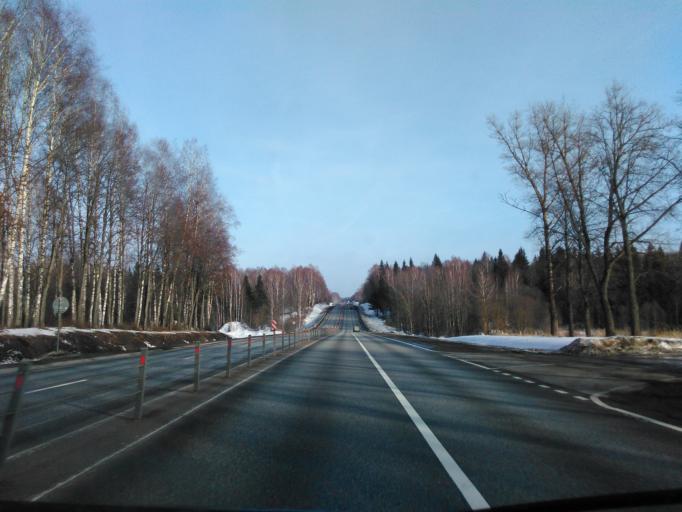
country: RU
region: Smolensk
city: Vyaz'ma
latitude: 55.1892
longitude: 34.0204
